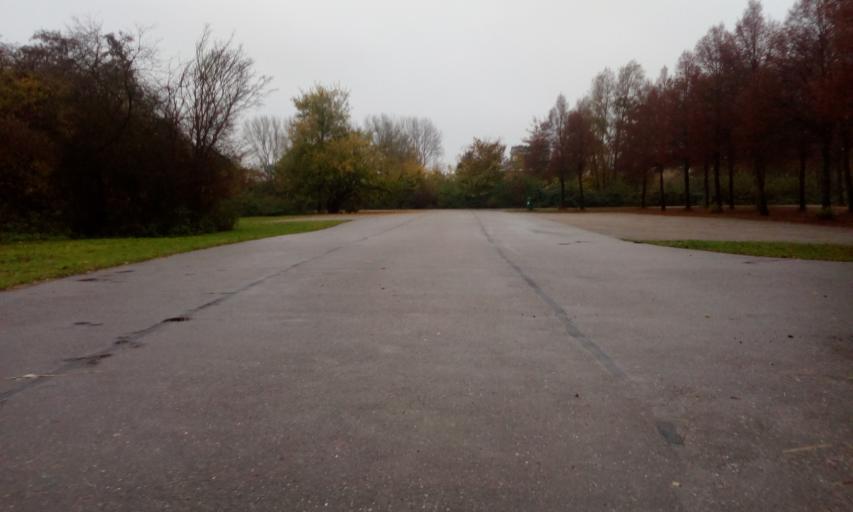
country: NL
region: South Holland
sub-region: Gemeente Lansingerland
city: Bergschenhoek
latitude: 51.9639
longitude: 4.5118
